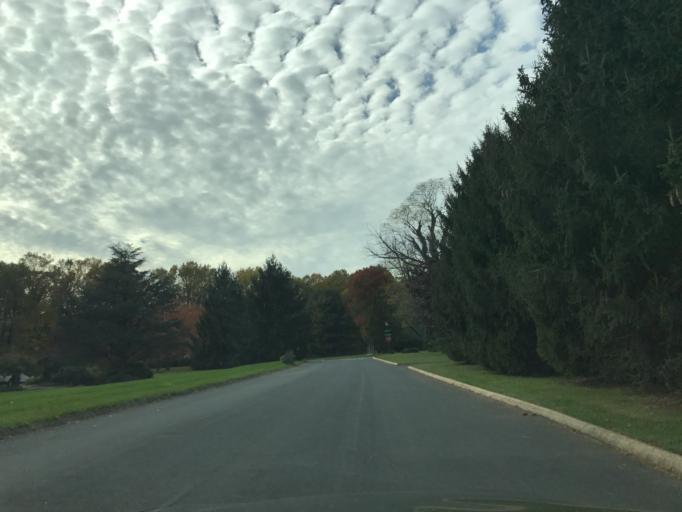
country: US
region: Maryland
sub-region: Harford County
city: Pleasant Hills
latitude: 39.4833
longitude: -76.3787
